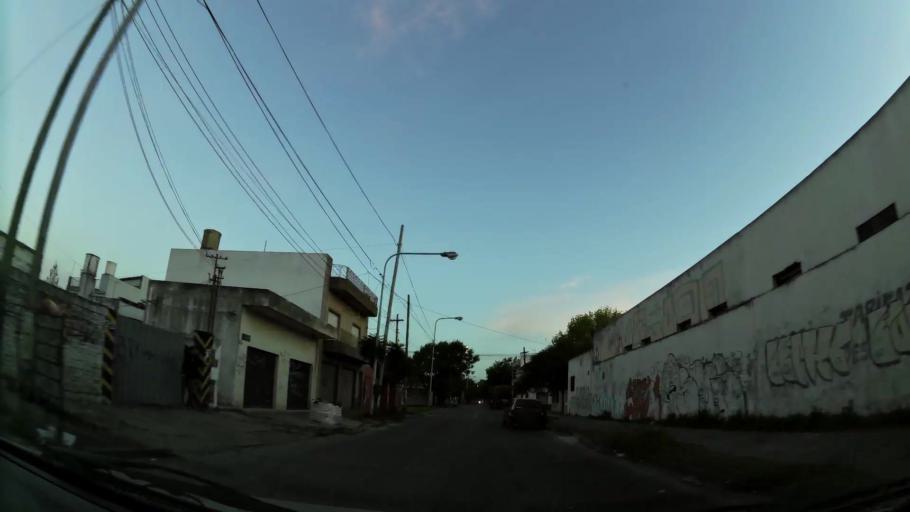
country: AR
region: Buenos Aires
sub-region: Partido de Quilmes
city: Quilmes
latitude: -34.7706
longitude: -58.1982
